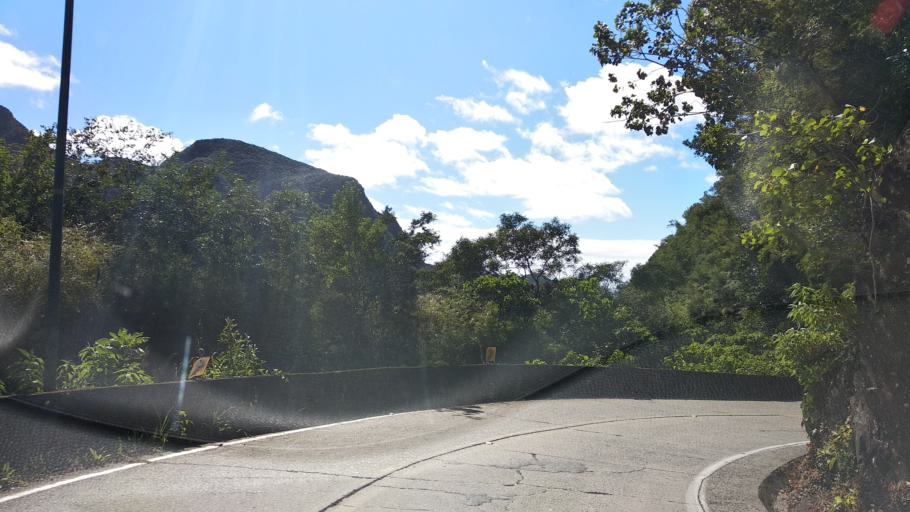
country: BR
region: Santa Catarina
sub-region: Lauro Muller
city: Lauro Muller
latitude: -28.3943
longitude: -49.5390
